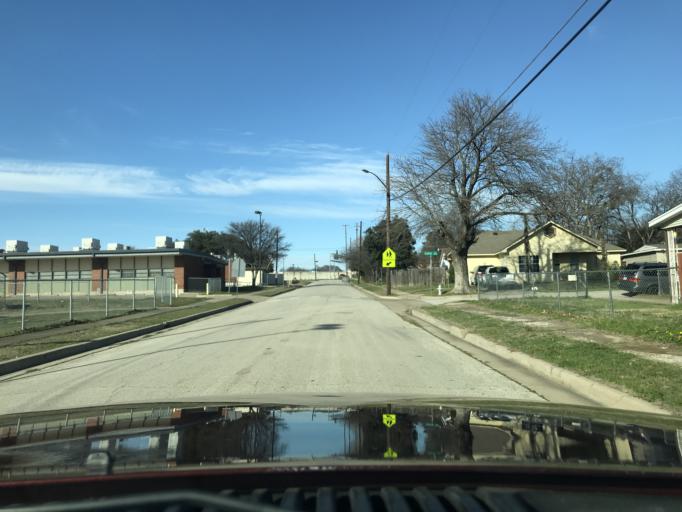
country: US
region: Texas
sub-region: Tarrant County
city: Edgecliff Village
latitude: 32.6629
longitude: -97.3437
